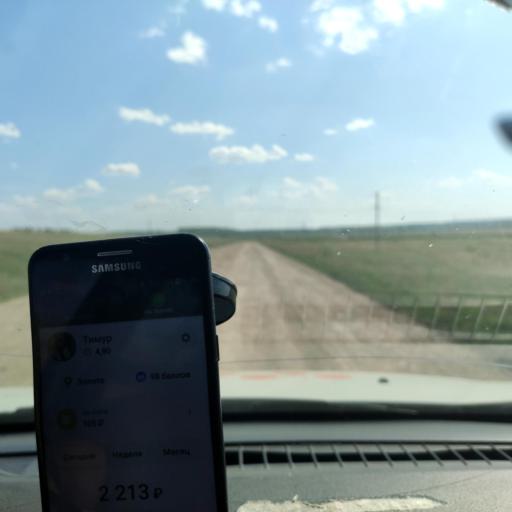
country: RU
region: Bashkortostan
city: Avdon
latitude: 54.5639
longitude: 55.6357
